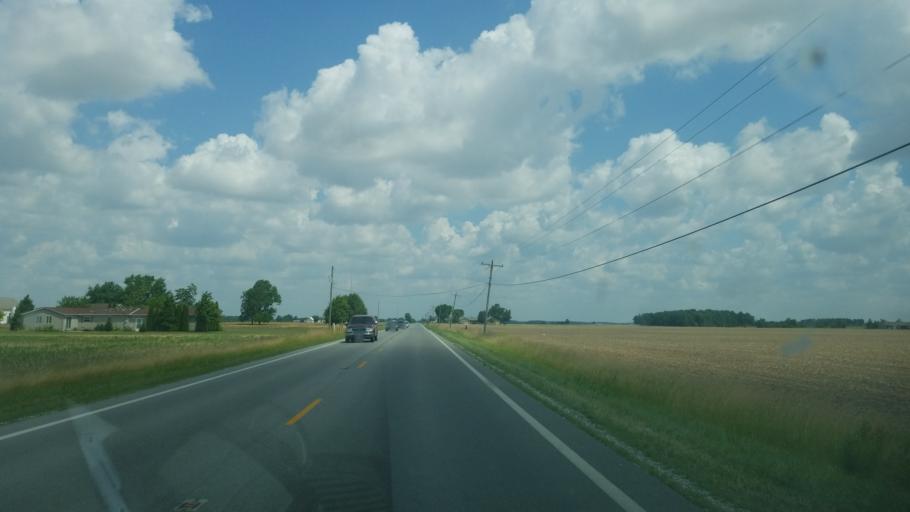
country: US
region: Ohio
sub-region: Auglaize County
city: Wapakoneta
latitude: 40.5943
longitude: -84.2029
